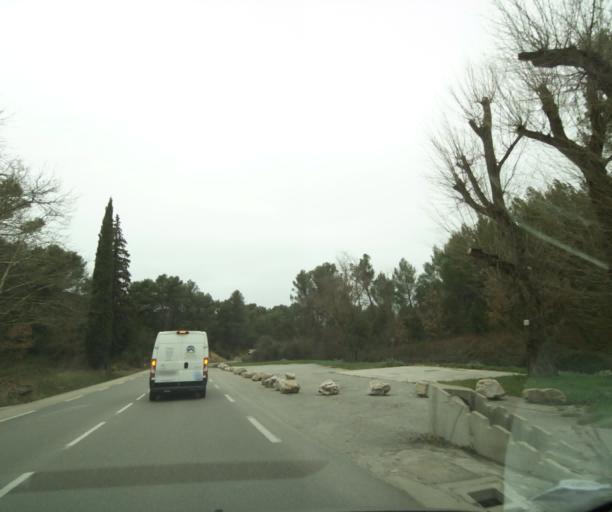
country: FR
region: Provence-Alpes-Cote d'Azur
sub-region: Departement des Bouches-du-Rhone
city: Fuveau
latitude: 43.4654
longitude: 5.5458
